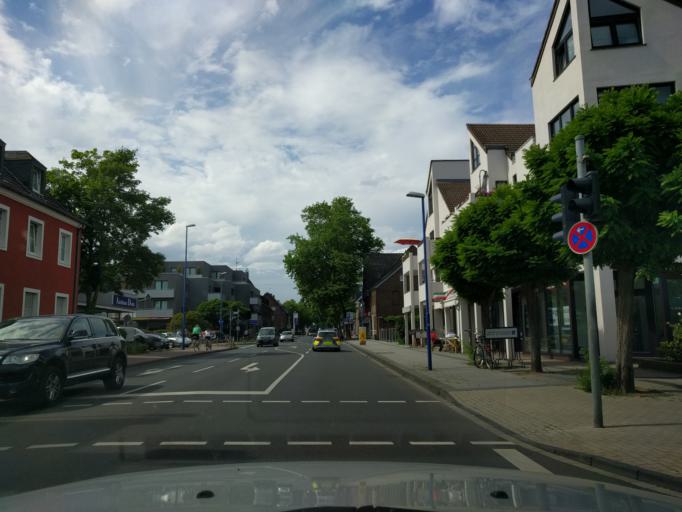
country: DE
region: North Rhine-Westphalia
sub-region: Regierungsbezirk Dusseldorf
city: Meerbusch
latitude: 51.2484
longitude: 6.6929
